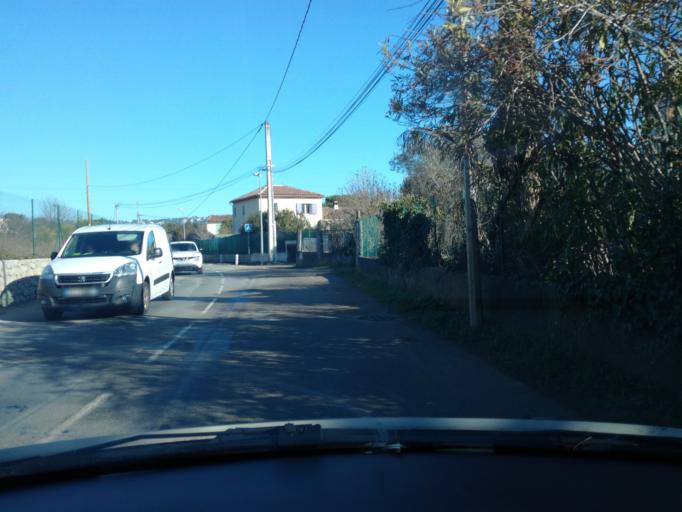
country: FR
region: Provence-Alpes-Cote d'Azur
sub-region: Departement des Alpes-Maritimes
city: La Roquette-sur-Siagne
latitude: 43.6027
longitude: 6.9528
